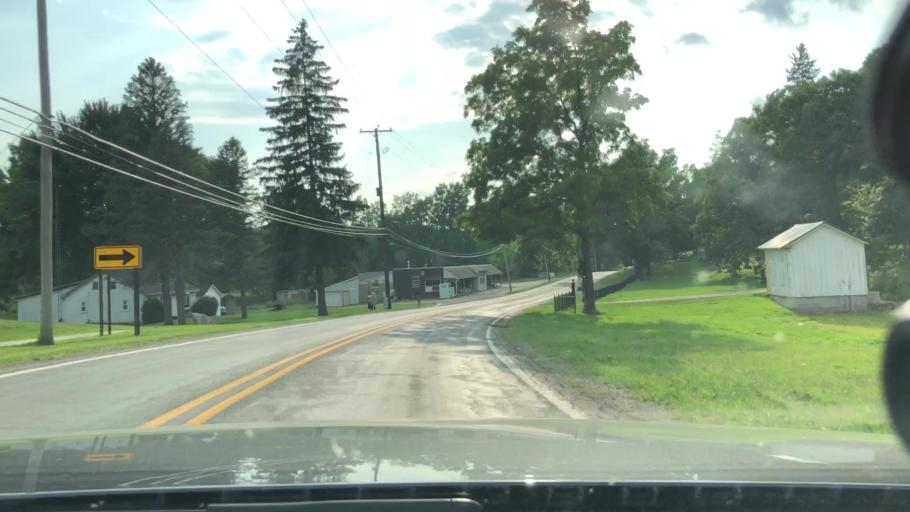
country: US
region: Michigan
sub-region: Washtenaw County
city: Manchester
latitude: 42.1446
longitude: -84.0528
